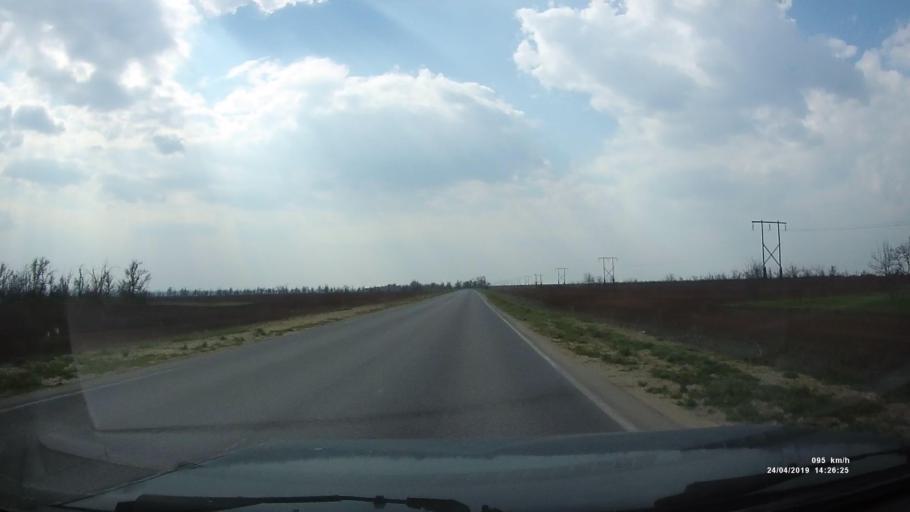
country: RU
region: Kalmykiya
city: Arshan'
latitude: 46.3337
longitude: 44.0631
